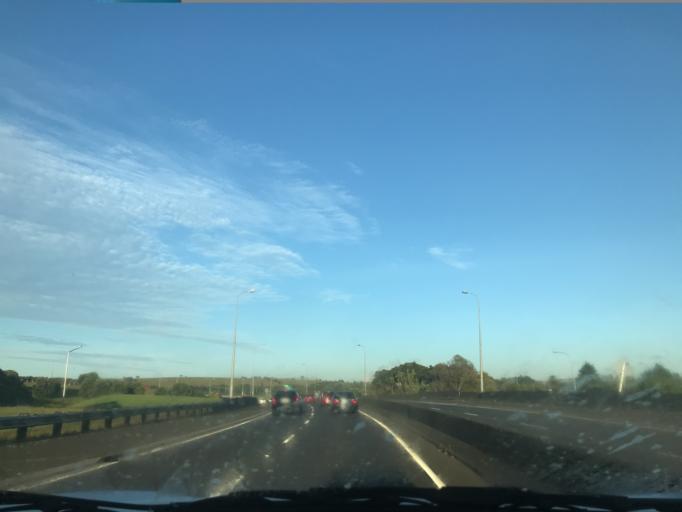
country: NZ
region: Auckland
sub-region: Auckland
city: Tamaki
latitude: -36.9159
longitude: 174.8374
